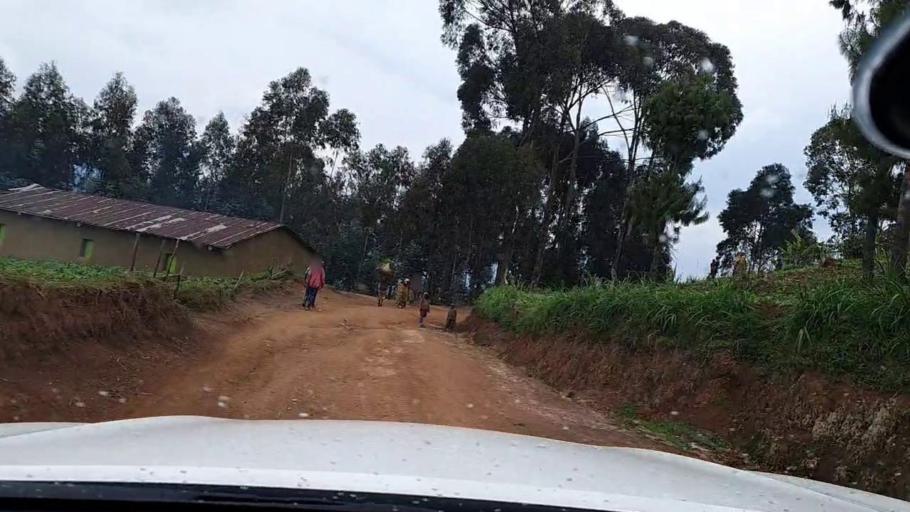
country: RW
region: Southern Province
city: Nzega
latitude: -2.3813
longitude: 29.2413
